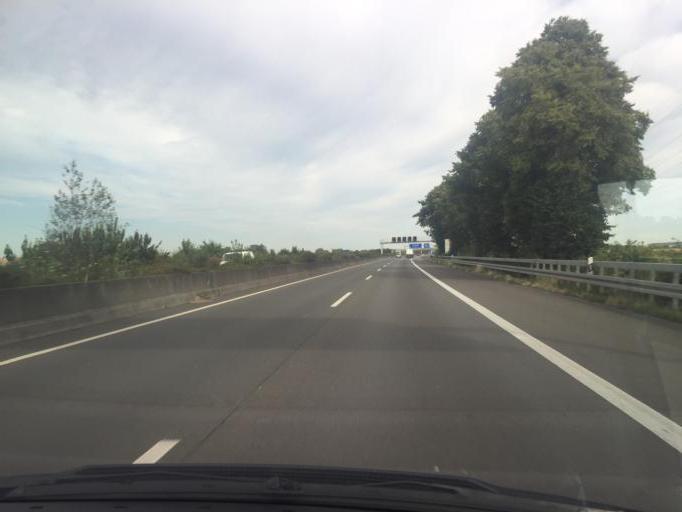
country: DE
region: North Rhine-Westphalia
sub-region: Regierungsbezirk Dusseldorf
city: Dusseldorf
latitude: 51.1451
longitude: 6.7652
